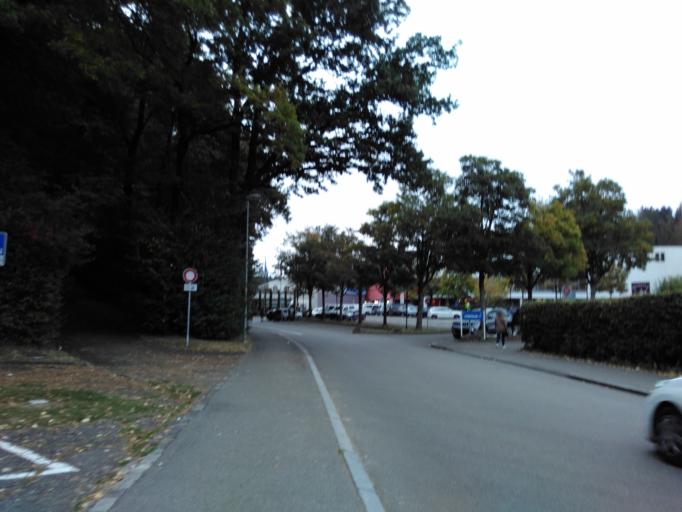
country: CH
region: Zurich
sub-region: Bezirk Buelach
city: Kloten / Spitz
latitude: 47.4452
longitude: 8.5819
